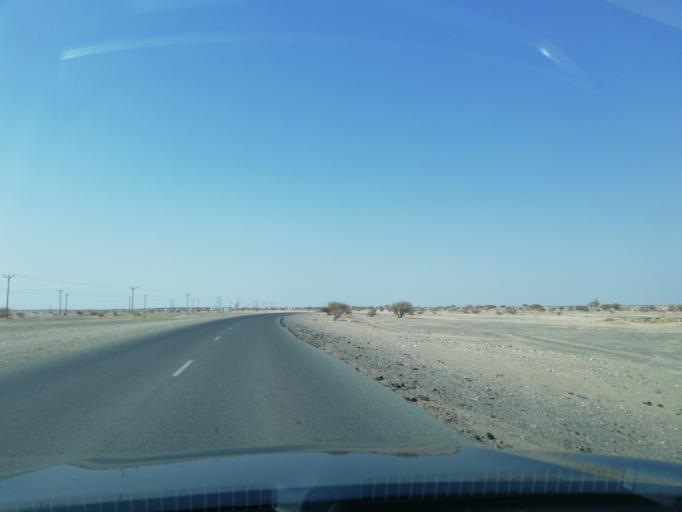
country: OM
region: Muhafazat ad Dakhiliyah
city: Adam
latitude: 22.3295
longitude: 58.0672
